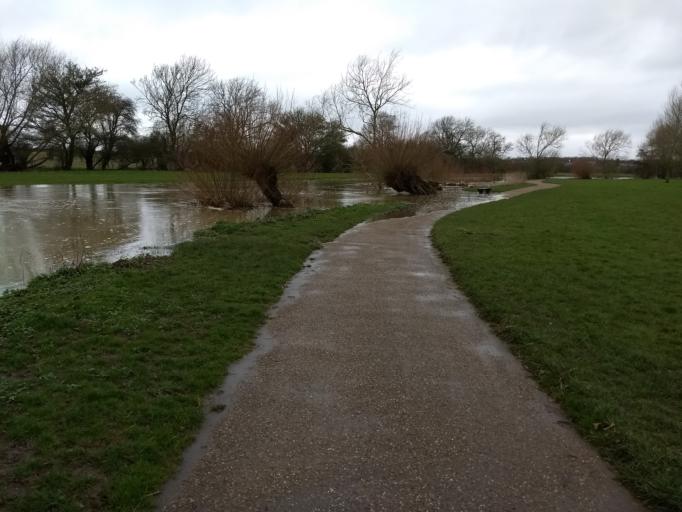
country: GB
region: England
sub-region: Milton Keynes
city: Stony Stratford
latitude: 52.0538
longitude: -0.8589
